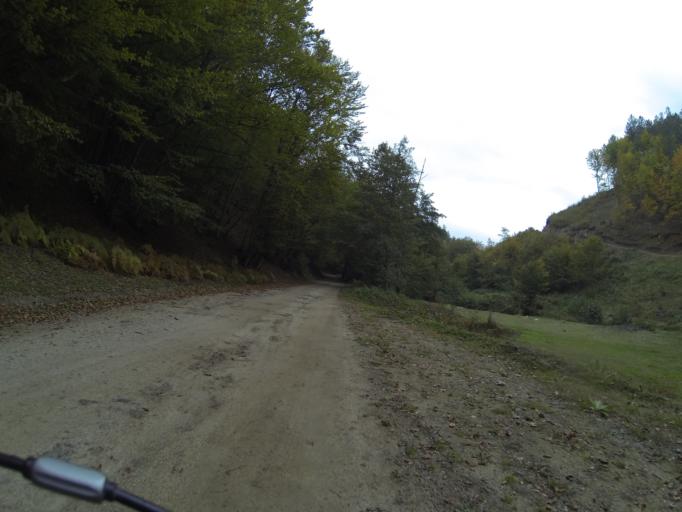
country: RO
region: Gorj
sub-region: Comuna Tismana
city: Sohodol
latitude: 45.0627
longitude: 22.8955
